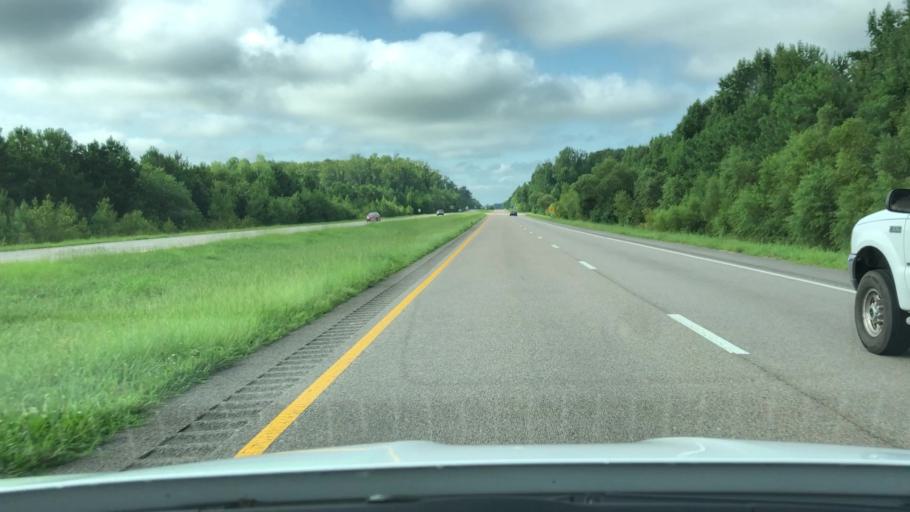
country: US
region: Virginia
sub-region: City of Portsmouth
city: Portsmouth Heights
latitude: 36.6405
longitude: -76.3621
